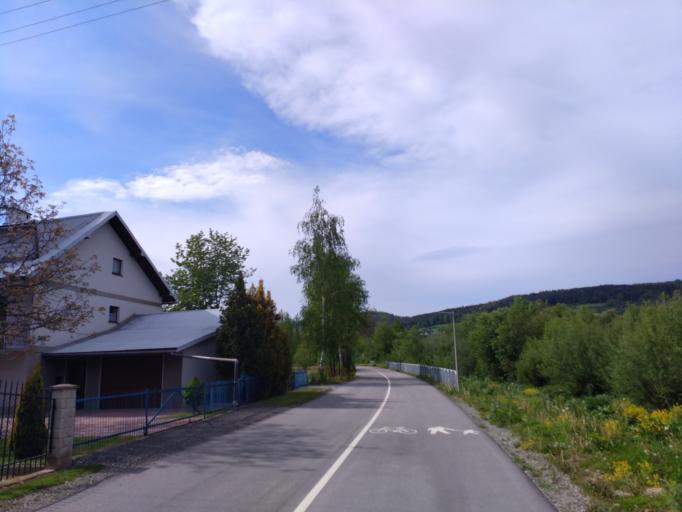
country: PL
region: Lesser Poland Voivodeship
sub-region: Powiat nowosadecki
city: Lacko
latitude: 49.5693
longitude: 20.4284
